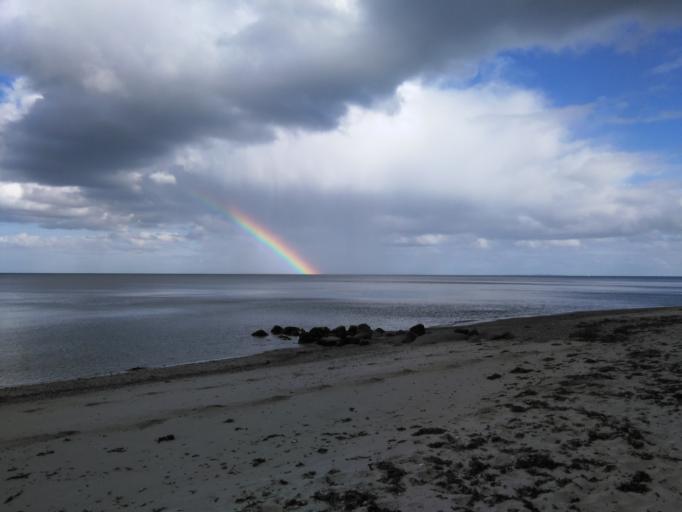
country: DK
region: Central Jutland
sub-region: Arhus Kommune
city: Beder
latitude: 56.0683
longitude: 10.2577
